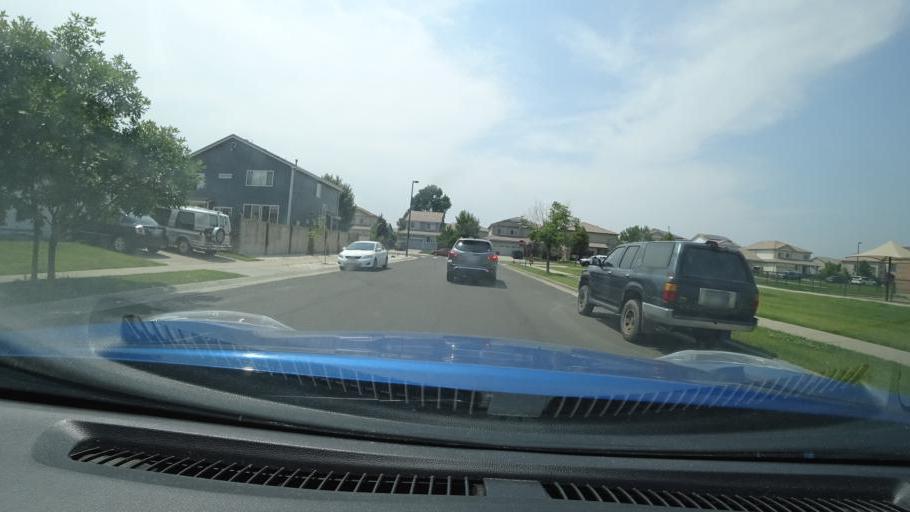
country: US
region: Colorado
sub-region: Adams County
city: Aurora
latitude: 39.7720
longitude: -104.7488
